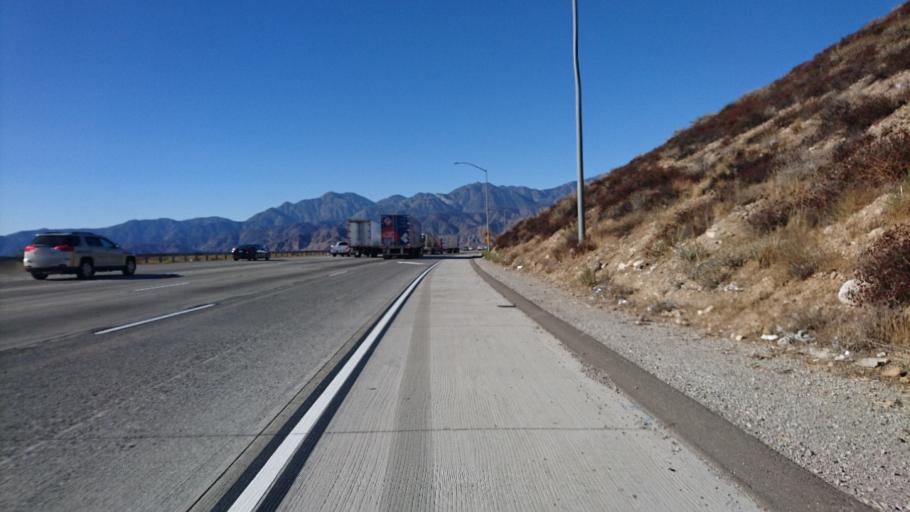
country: US
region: California
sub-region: San Bernardino County
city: Oak Hills
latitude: 34.3468
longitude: -117.4500
